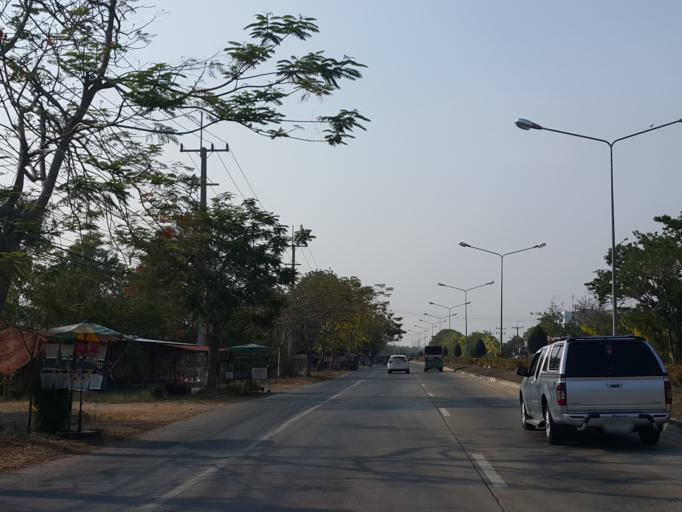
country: TH
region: Suphan Buri
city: Sam Chuk
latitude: 14.7604
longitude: 100.0950
